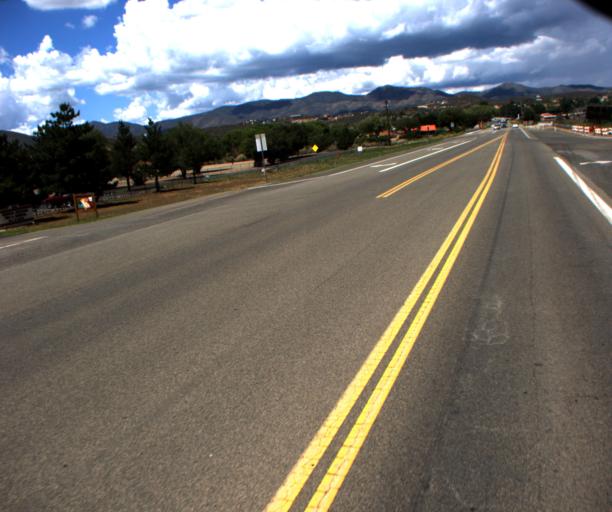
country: US
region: Arizona
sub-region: Yavapai County
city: Dewey-Humboldt
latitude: 34.5297
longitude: -112.2350
